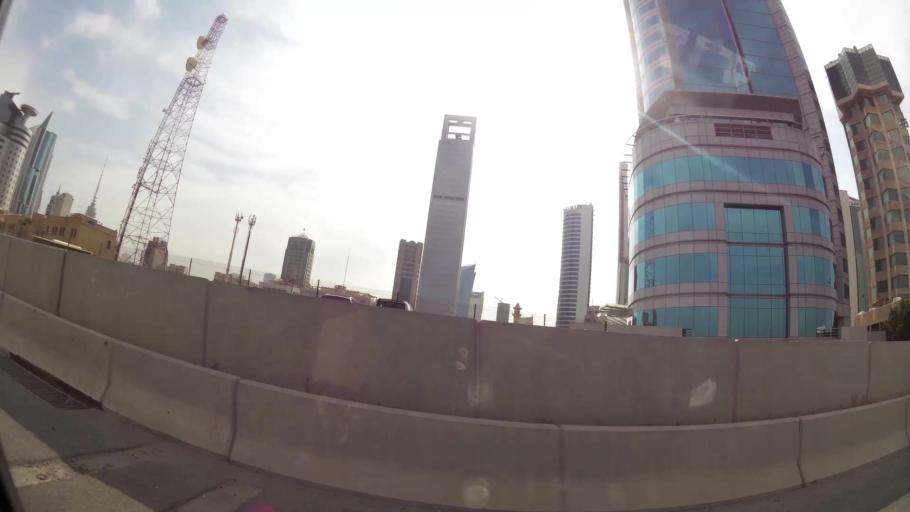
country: KW
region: Al Asimah
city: Ash Shamiyah
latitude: 29.3642
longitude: 47.9611
